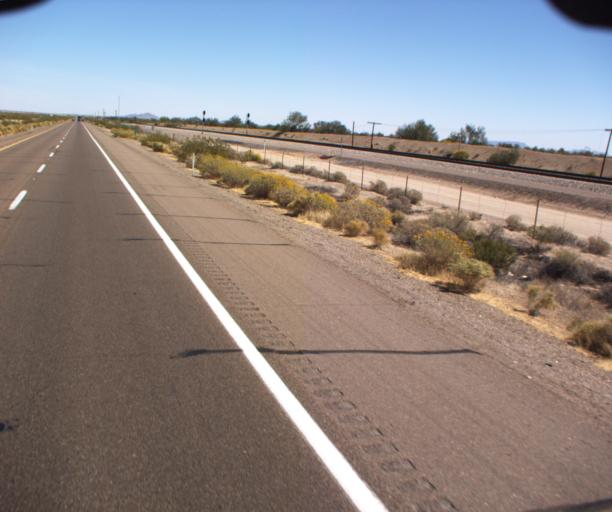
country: US
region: Arizona
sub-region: Yuma County
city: Wellton
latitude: 32.7347
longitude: -113.7031
